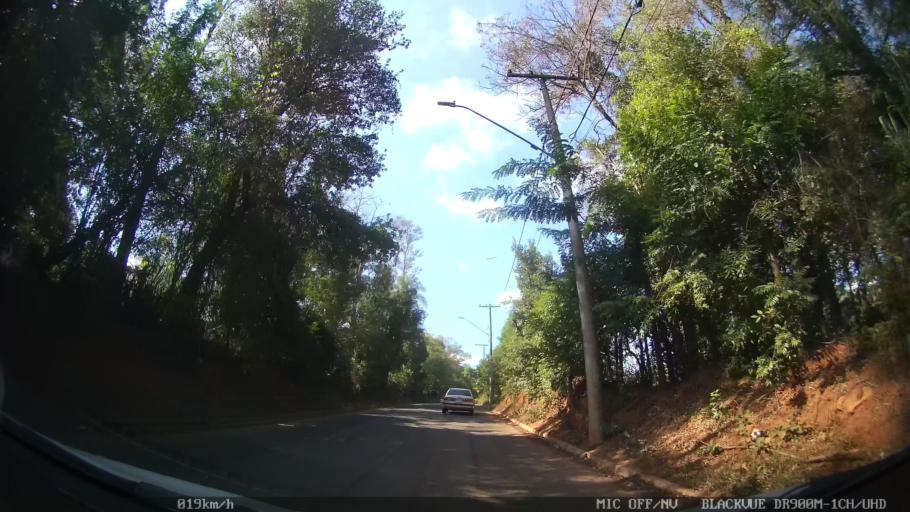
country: BR
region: Sao Paulo
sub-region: Hortolandia
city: Hortolandia
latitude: -22.8735
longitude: -47.2380
